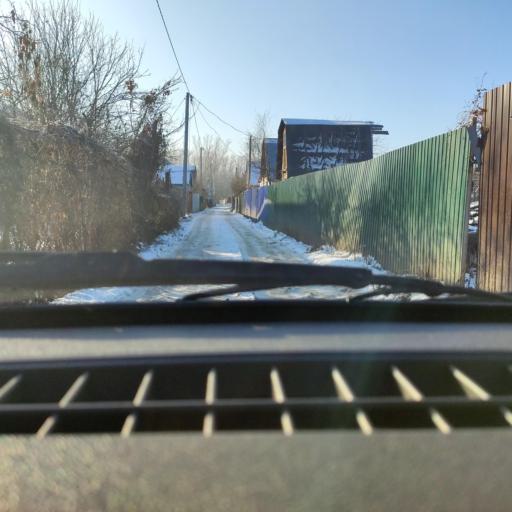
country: RU
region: Bashkortostan
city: Ufa
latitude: 54.7713
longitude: 55.9390
